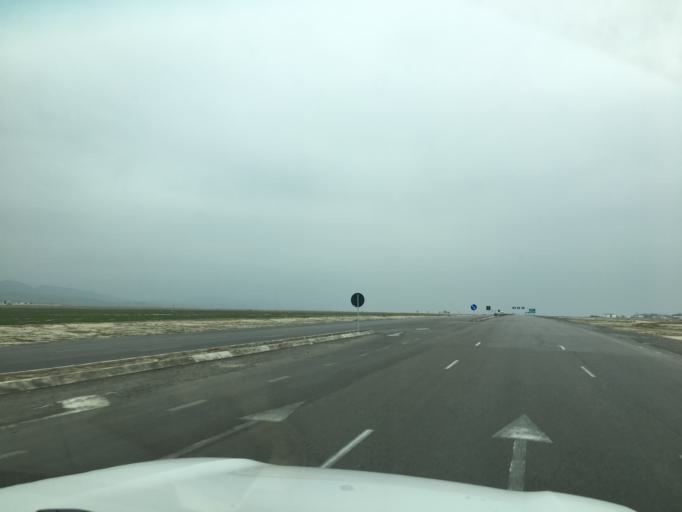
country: IR
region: Razavi Khorasan
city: Dargaz
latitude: 37.7156
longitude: 59.0188
